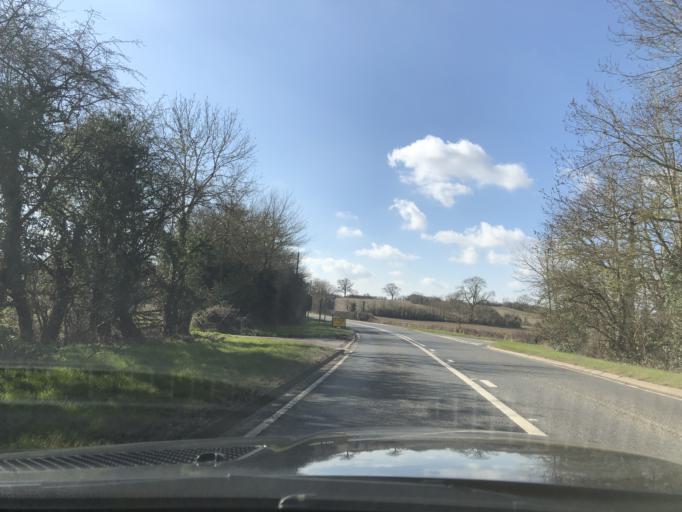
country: GB
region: England
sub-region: Warwickshire
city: Long Itchington
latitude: 52.3133
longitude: -1.4303
